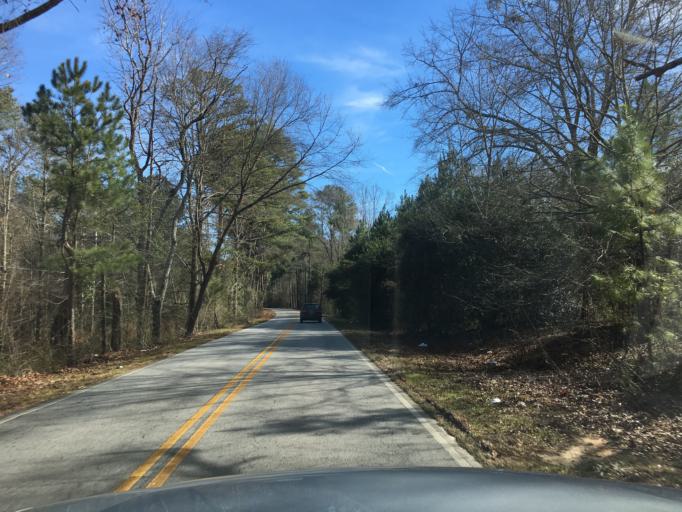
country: US
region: Georgia
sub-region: Rockdale County
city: Lakeview Estates
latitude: 33.7543
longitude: -84.0433
